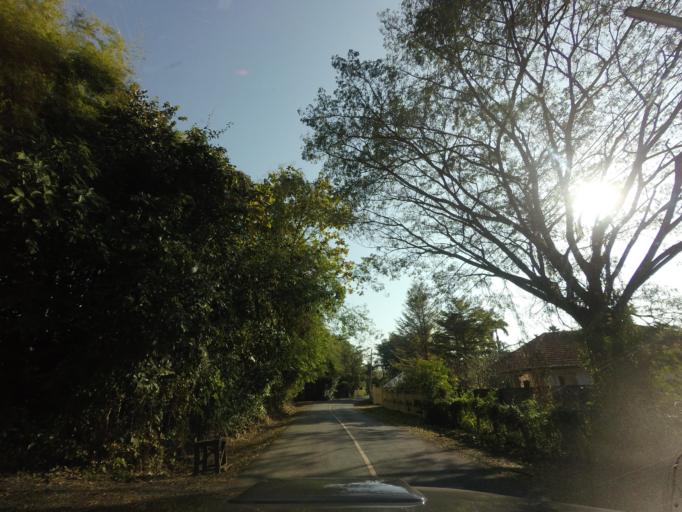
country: TH
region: Chiang Mai
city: San Sai
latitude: 18.9179
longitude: 99.1377
